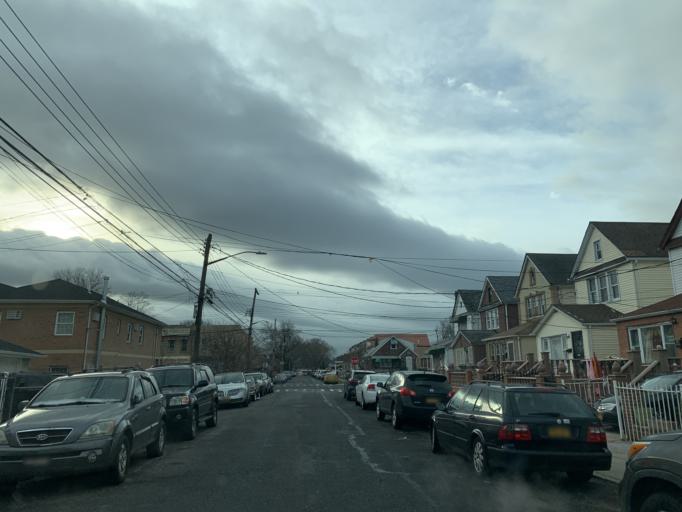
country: US
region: New York
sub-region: Queens County
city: Jamaica
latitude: 40.6842
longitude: -73.8109
